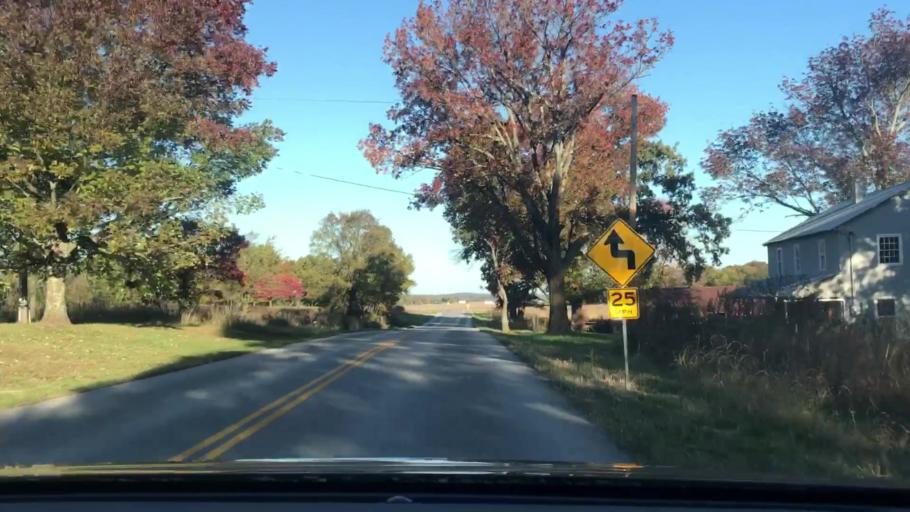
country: US
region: Kentucky
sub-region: Logan County
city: Auburn
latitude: 36.8271
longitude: -86.6757
